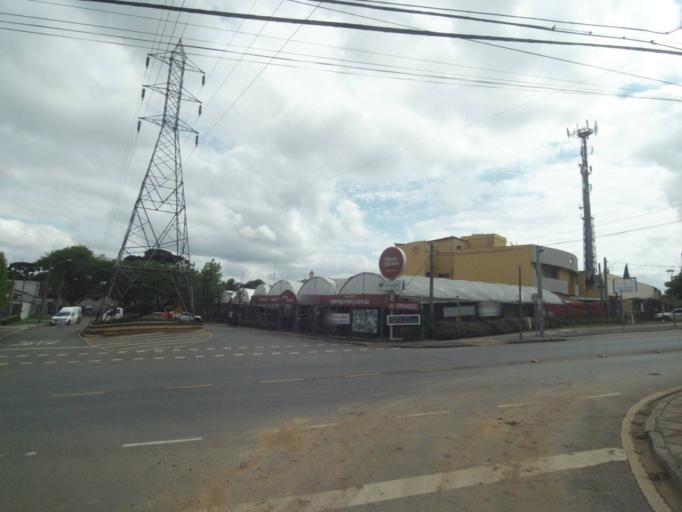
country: BR
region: Parana
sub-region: Curitiba
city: Curitiba
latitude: -25.3853
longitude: -49.2797
